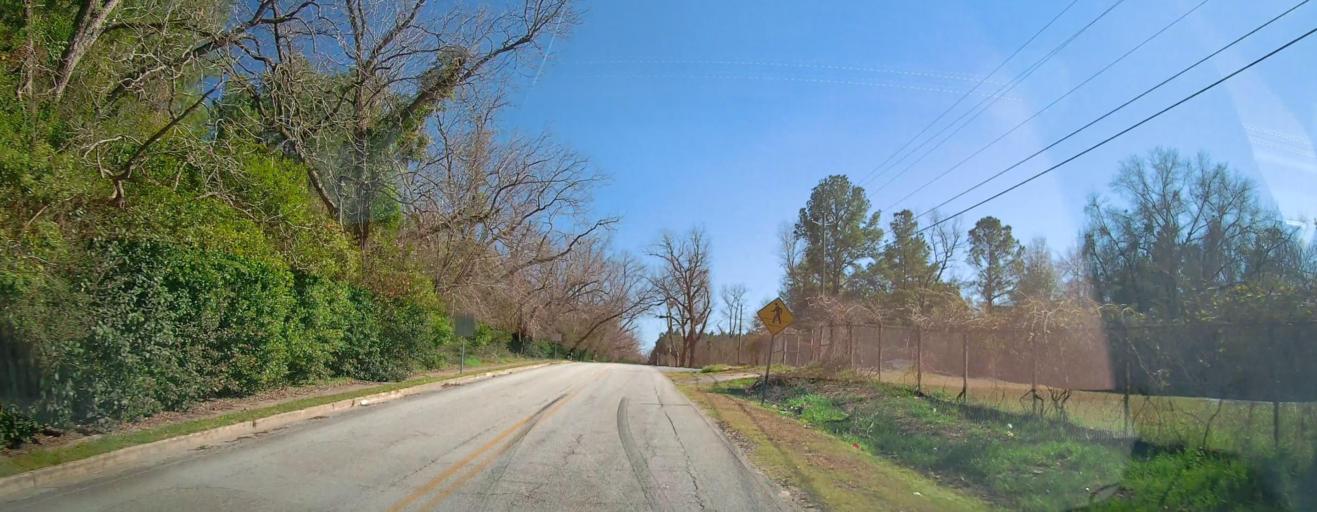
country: US
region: Georgia
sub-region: Macon County
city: Montezuma
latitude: 32.2831
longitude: -84.0306
